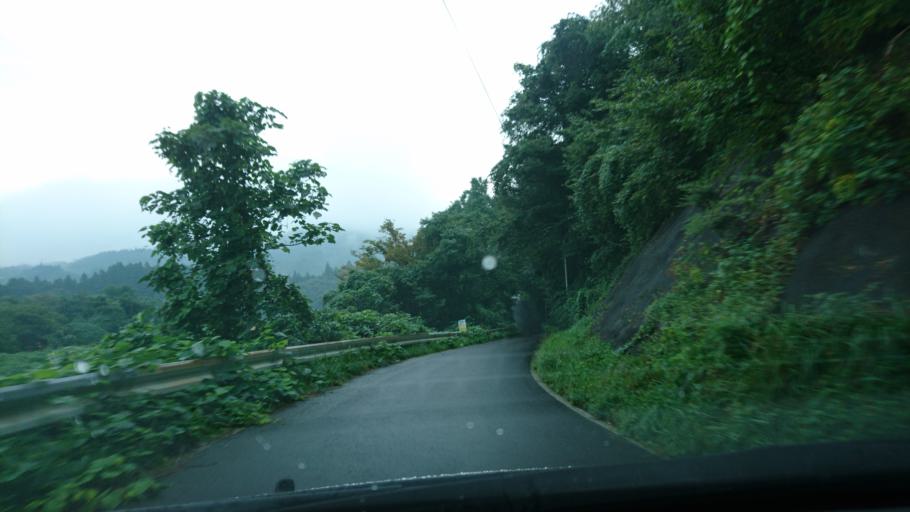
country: JP
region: Iwate
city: Ichinoseki
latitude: 38.8791
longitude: 141.2575
